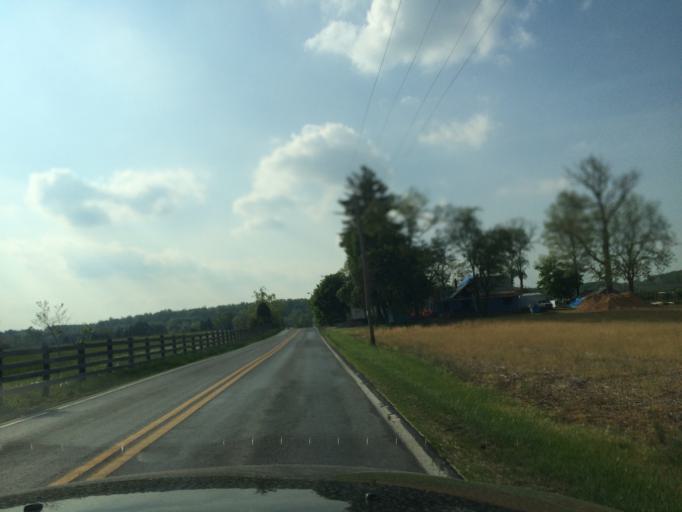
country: US
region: Maryland
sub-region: Carroll County
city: Mount Airy
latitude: 39.3054
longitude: -77.1020
